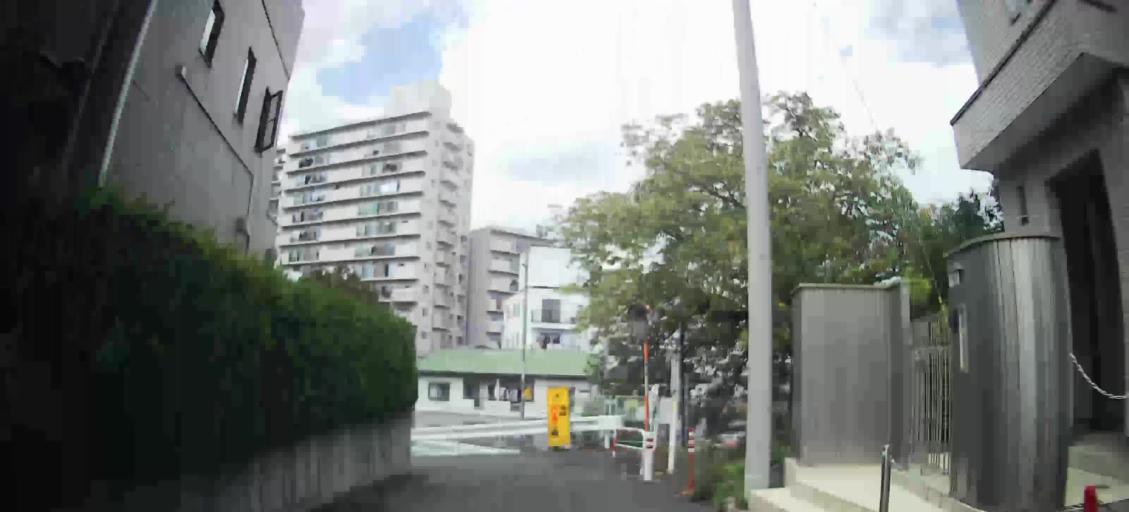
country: JP
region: Kanagawa
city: Yokohama
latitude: 35.4767
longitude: 139.5488
